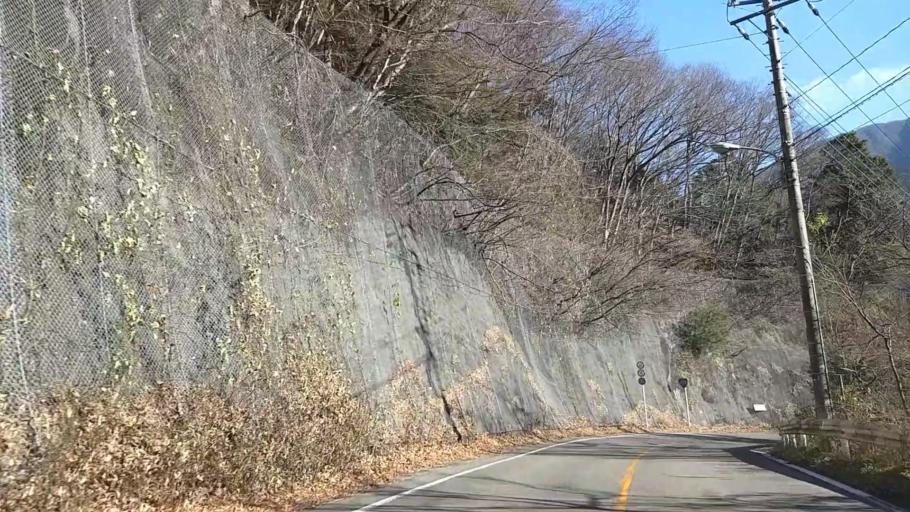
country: JP
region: Yamanashi
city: Uenohara
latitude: 35.5301
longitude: 139.1010
